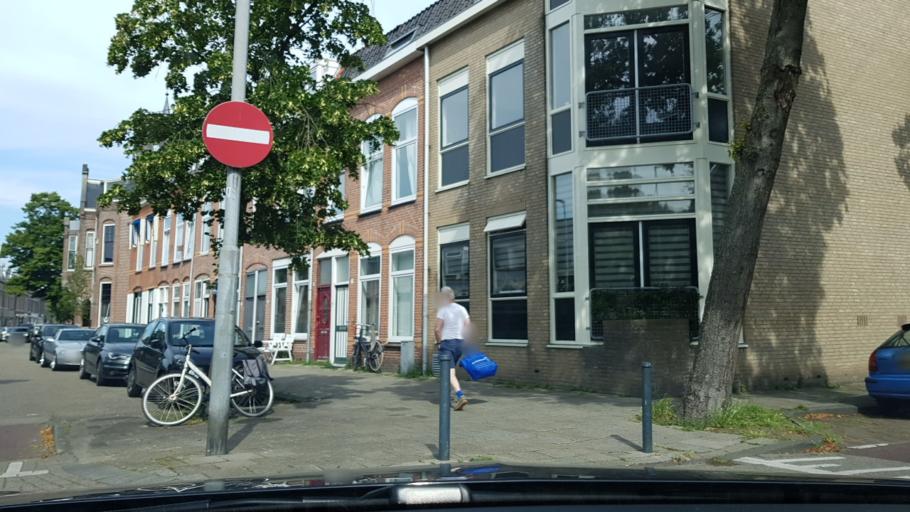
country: NL
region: North Holland
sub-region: Gemeente Haarlem
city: Haarlem
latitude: 52.3924
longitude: 4.6440
